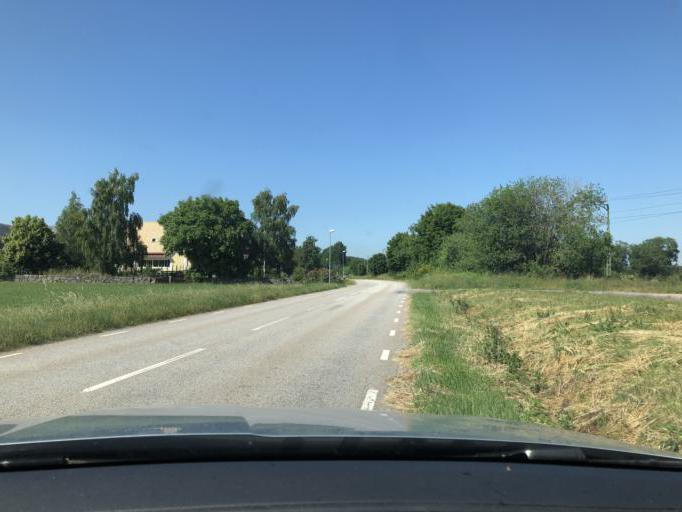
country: SE
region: Blekinge
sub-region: Solvesborgs Kommun
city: Soelvesborg
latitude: 56.1049
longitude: 14.6192
